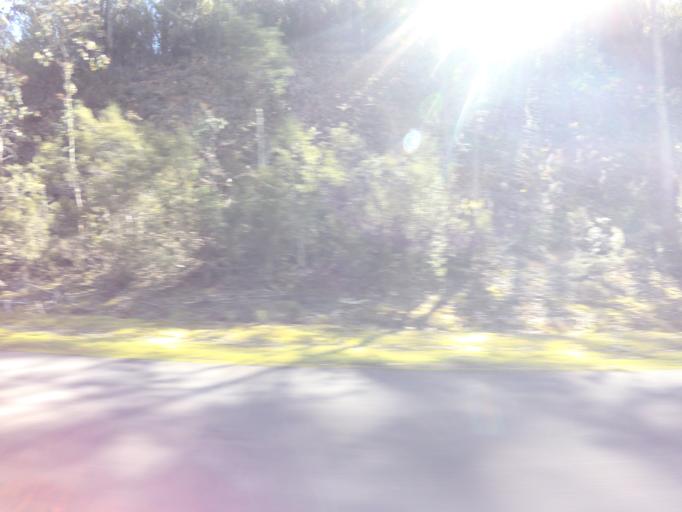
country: AU
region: Tasmania
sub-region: Derwent Valley
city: New Norfolk
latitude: -42.7393
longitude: 146.4960
